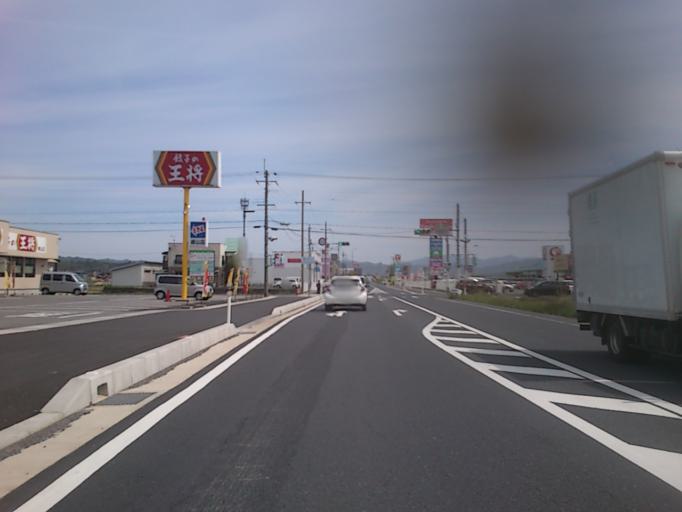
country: JP
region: Kyoto
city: Miyazu
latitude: 35.6182
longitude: 135.0758
